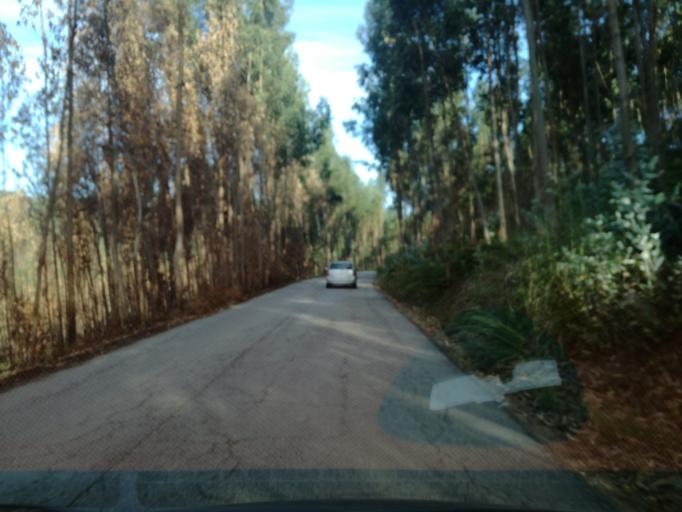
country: PT
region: Porto
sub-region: Valongo
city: Alfena
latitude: 41.2626
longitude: -8.5234
